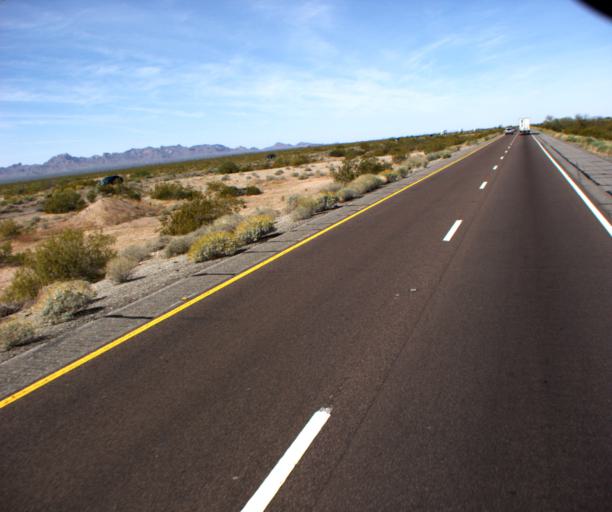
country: US
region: Arizona
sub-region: La Paz County
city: Salome
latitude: 33.5535
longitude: -113.2490
